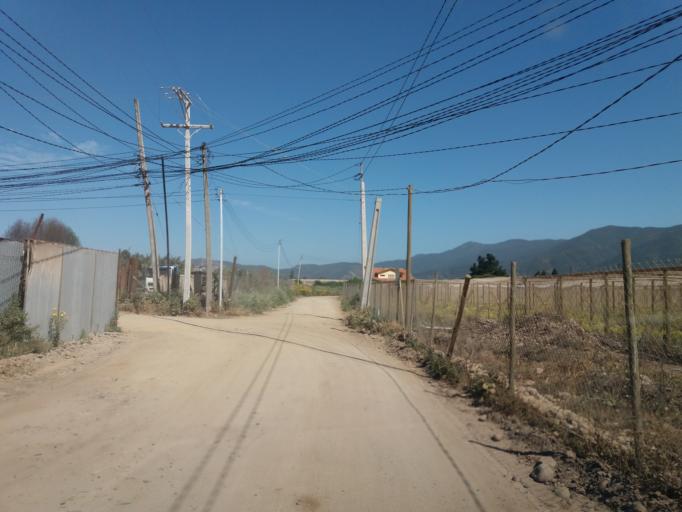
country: CL
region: Valparaiso
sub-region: Provincia de Quillota
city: Quillota
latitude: -32.8748
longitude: -71.2249
